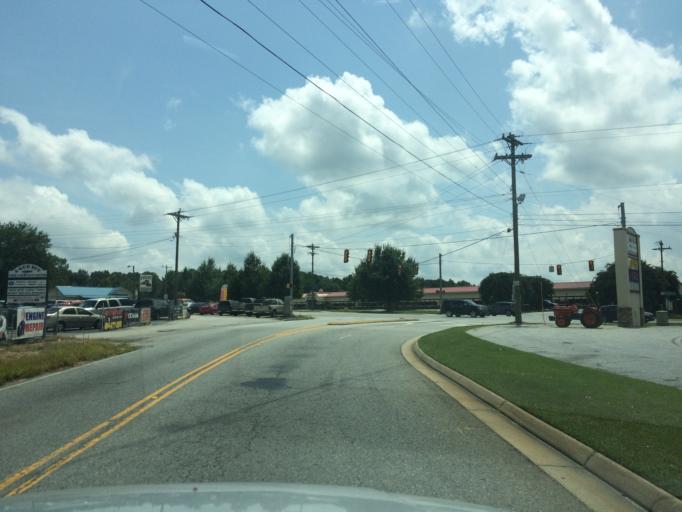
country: US
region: South Carolina
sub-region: Spartanburg County
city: Duncan
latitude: 34.8840
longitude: -82.1499
